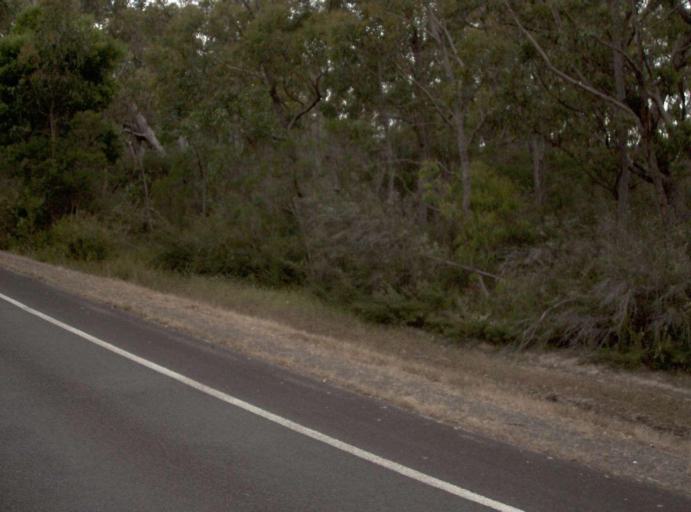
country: AU
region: Victoria
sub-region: Wellington
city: Sale
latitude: -38.5032
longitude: 146.8959
